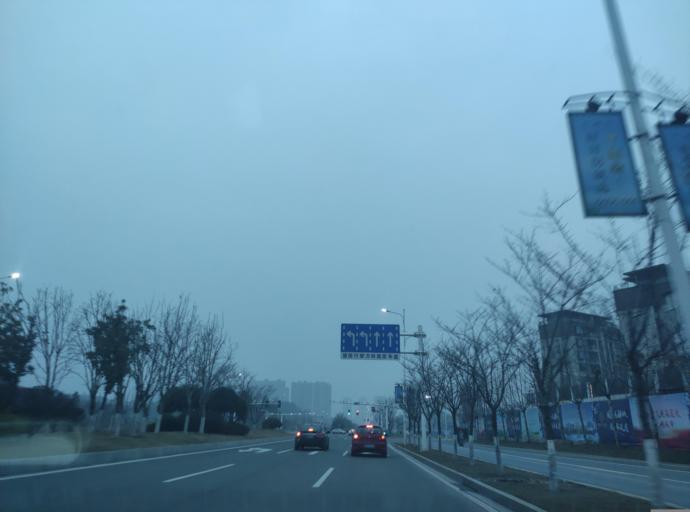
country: CN
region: Jiangxi Sheng
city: Pingxiang
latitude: 27.6693
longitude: 113.8506
